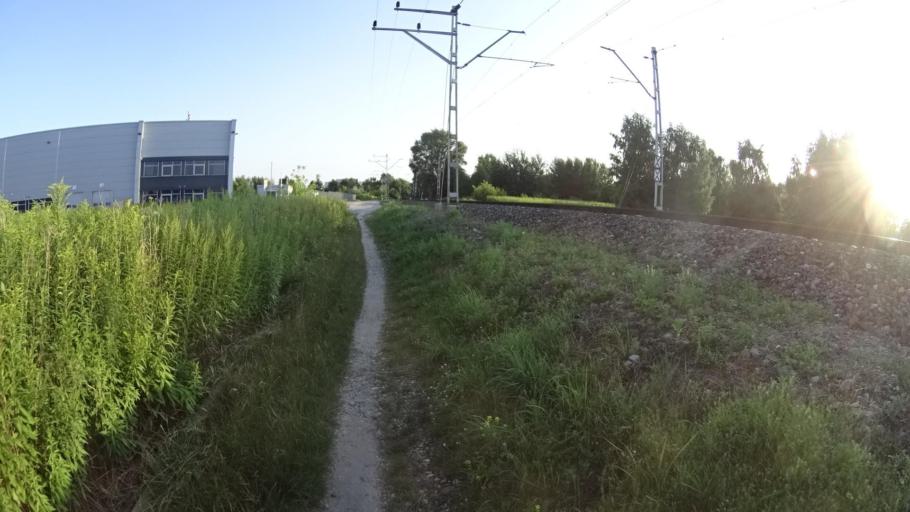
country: PL
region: Masovian Voivodeship
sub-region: Warszawa
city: Wlochy
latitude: 52.1886
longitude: 20.9285
